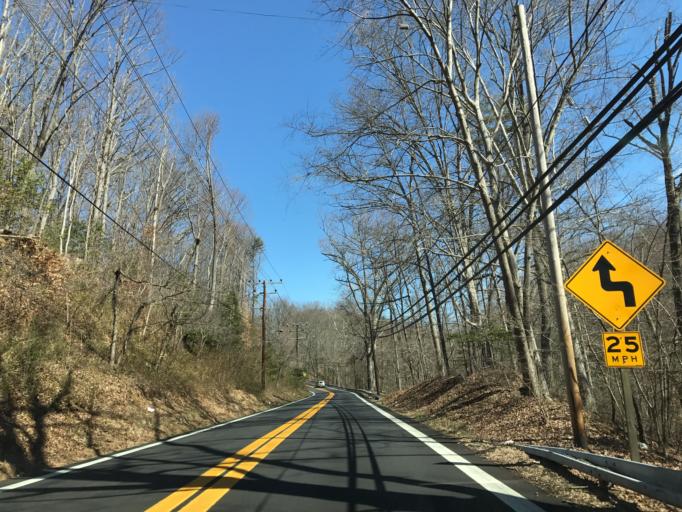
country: US
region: Maryland
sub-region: Anne Arundel County
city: Naval Academy
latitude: 39.0101
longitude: -76.4745
